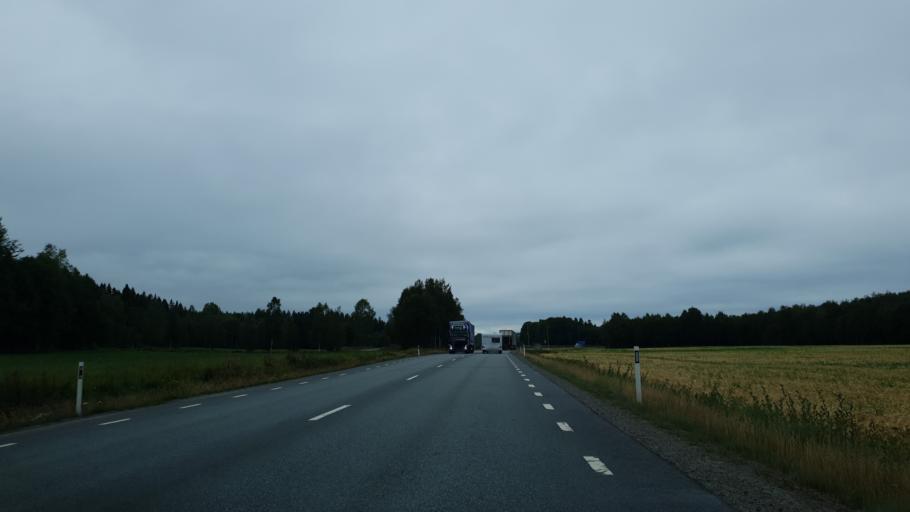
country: SE
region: Vaesterbotten
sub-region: Skelleftea Kommun
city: Burea
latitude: 64.3878
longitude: 21.2994
